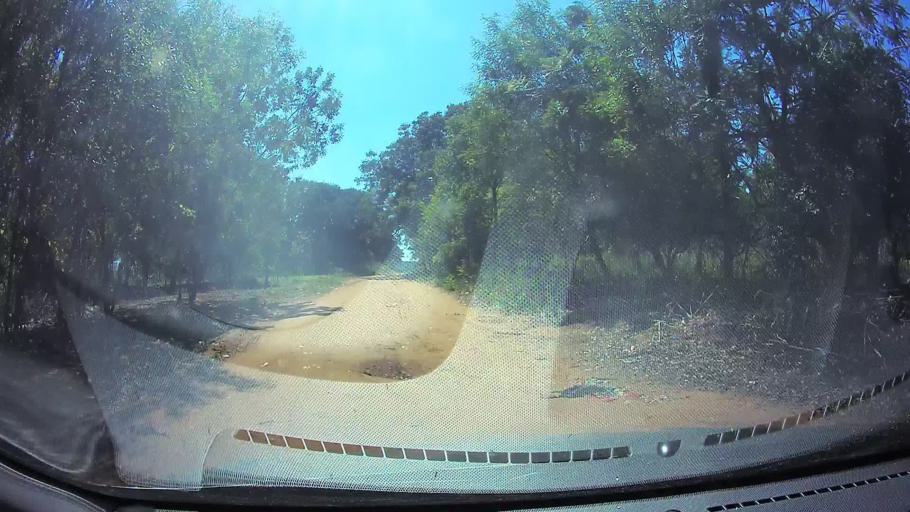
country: PY
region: Central
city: Limpio
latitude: -25.2422
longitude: -57.4547
